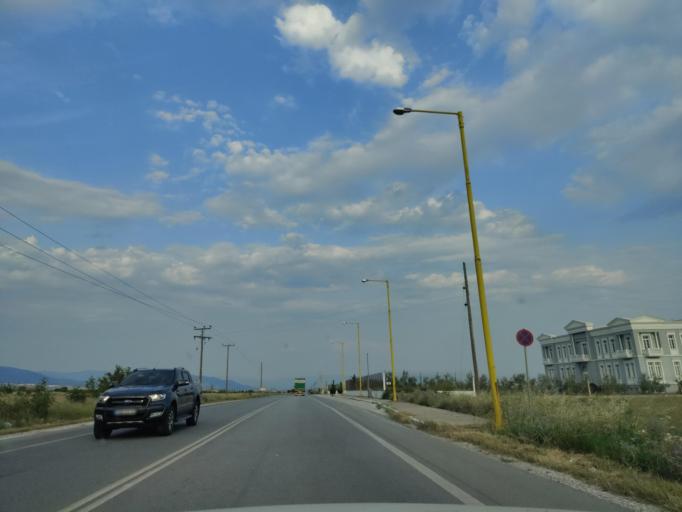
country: GR
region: East Macedonia and Thrace
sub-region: Nomos Dramas
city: Petroussa
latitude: 41.1759
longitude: 24.0093
